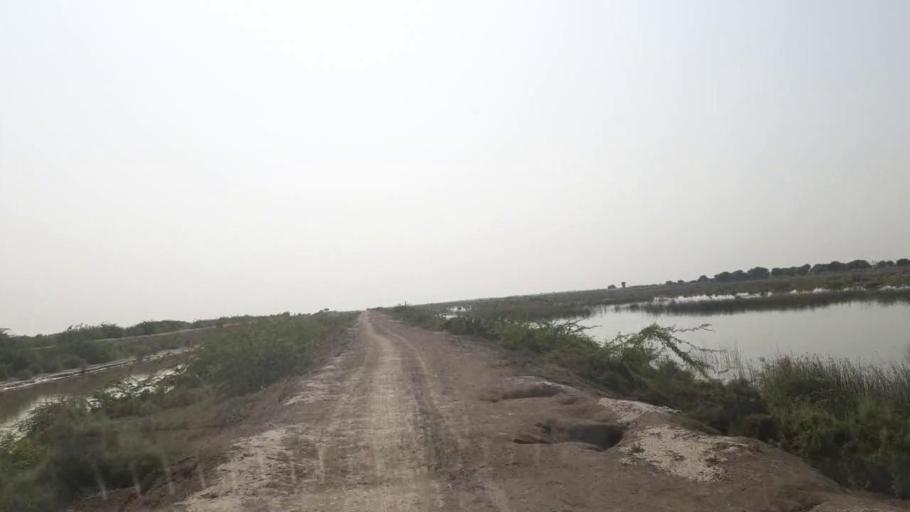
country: PK
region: Sindh
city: Kadhan
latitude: 24.3912
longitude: 68.9025
